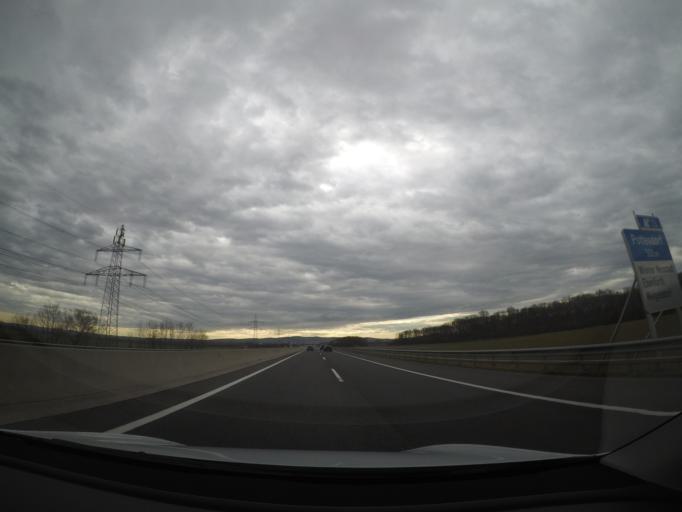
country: AT
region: Lower Austria
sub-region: Politischer Bezirk Baden
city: Ebreichsdorf
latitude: 47.9332
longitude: 16.3845
